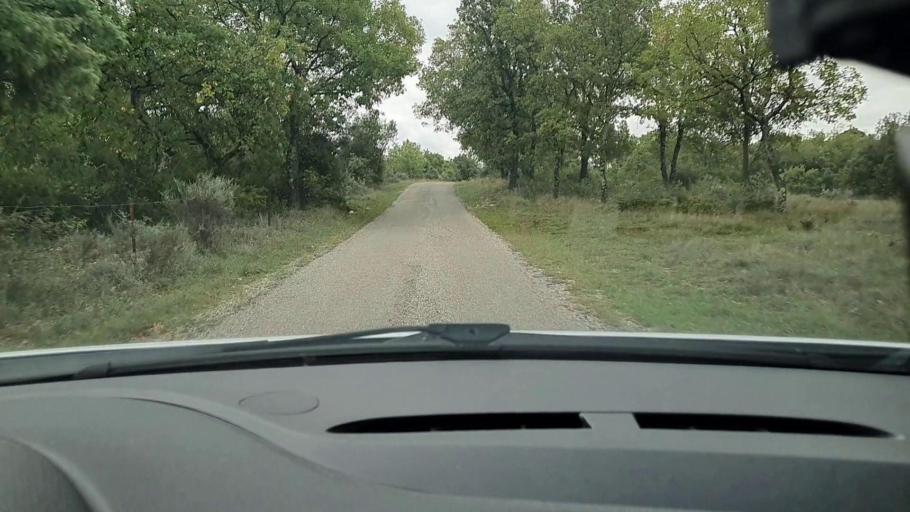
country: FR
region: Languedoc-Roussillon
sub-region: Departement du Gard
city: Mons
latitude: 44.1528
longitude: 4.2909
